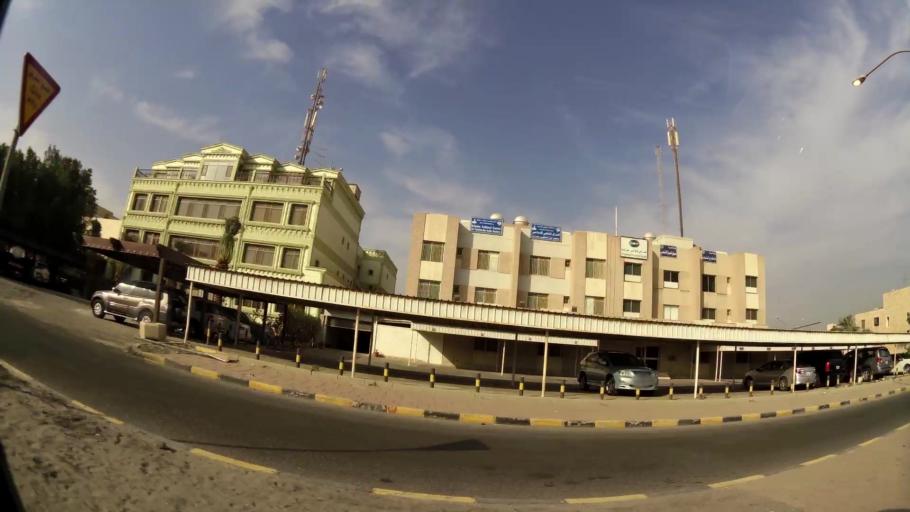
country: KW
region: Muhafazat Hawalli
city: Salwa
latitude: 29.2858
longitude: 48.0865
